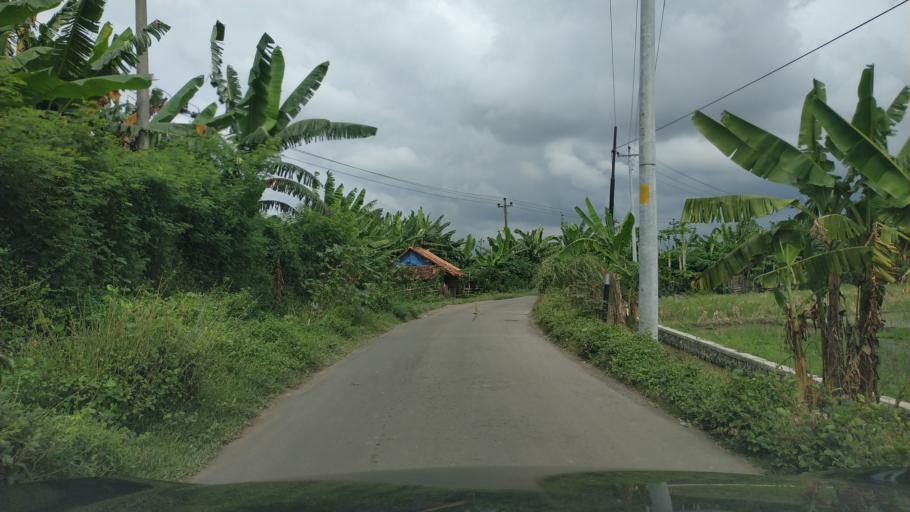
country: ID
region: Central Java
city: Pemalang
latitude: -6.9243
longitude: 109.3374
